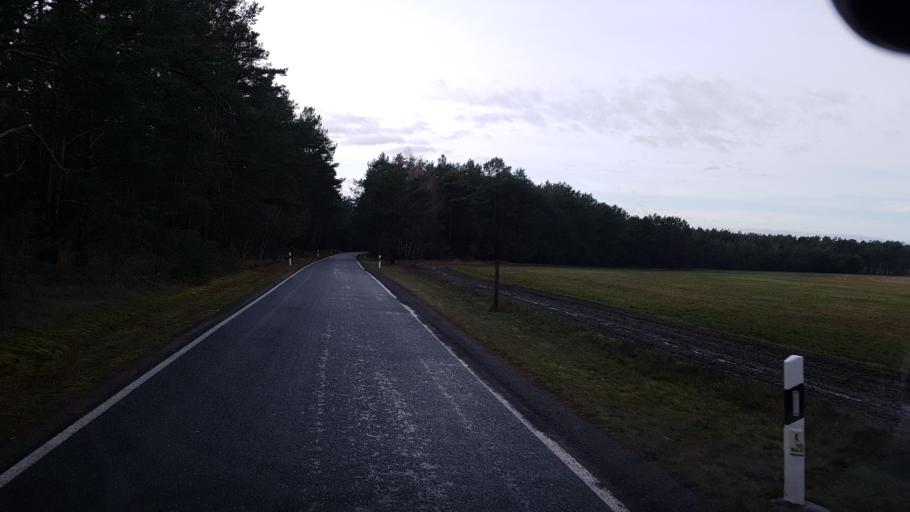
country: DE
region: Brandenburg
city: Bronkow
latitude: 51.6676
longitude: 13.9598
